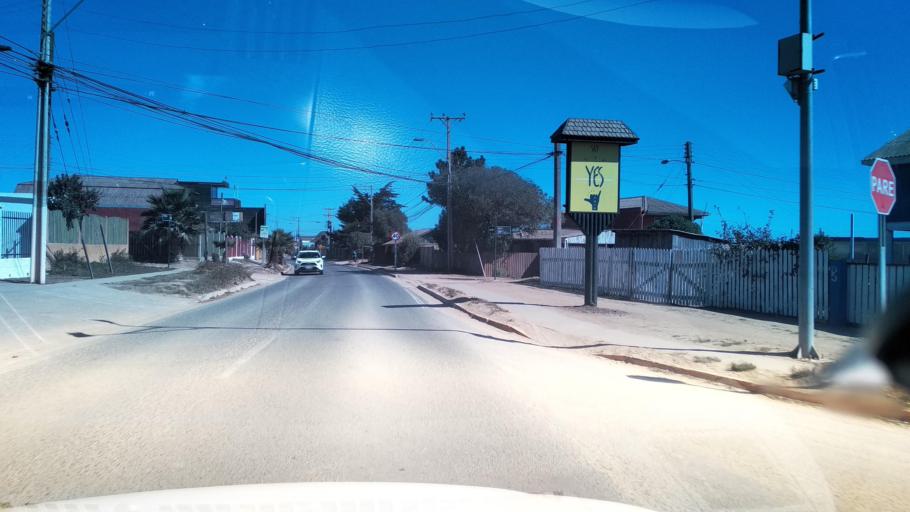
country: CL
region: O'Higgins
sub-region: Provincia de Colchagua
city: Santa Cruz
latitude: -34.3993
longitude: -72.0225
